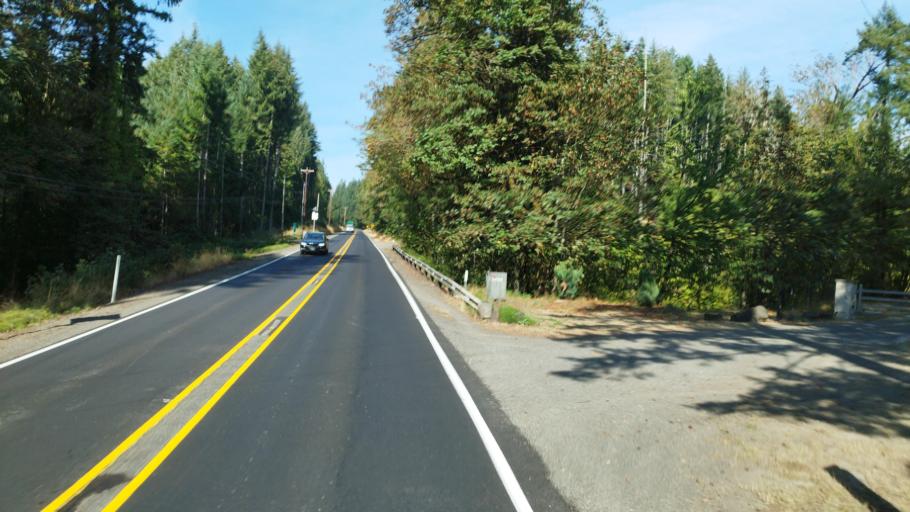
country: US
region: Oregon
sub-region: Washington County
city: Bethany
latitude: 45.6008
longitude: -122.8615
